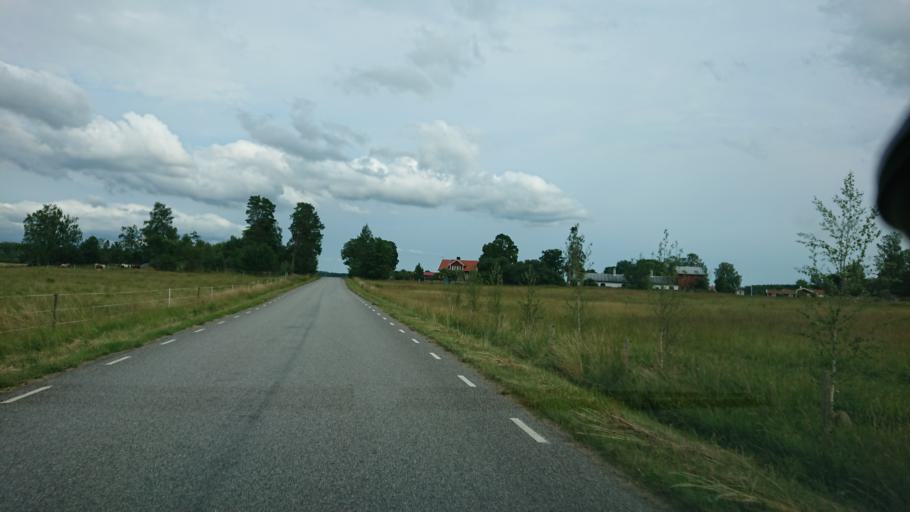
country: SE
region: Uppsala
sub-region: Osthammars Kommun
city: Bjorklinge
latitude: 59.9986
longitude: 17.4840
